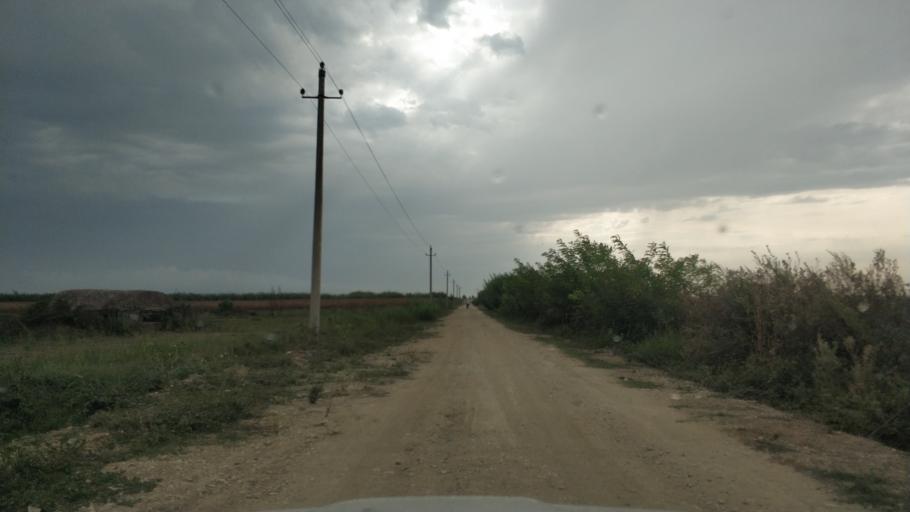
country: AL
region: Fier
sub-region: Rrethi i Fierit
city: Dermenas
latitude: 40.7150
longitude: 19.4527
